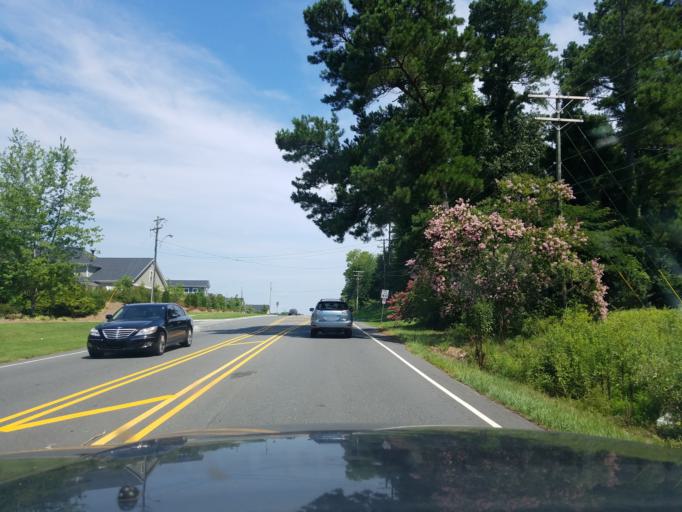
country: US
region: North Carolina
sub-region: Durham County
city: Durham
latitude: 35.9513
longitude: -78.9703
